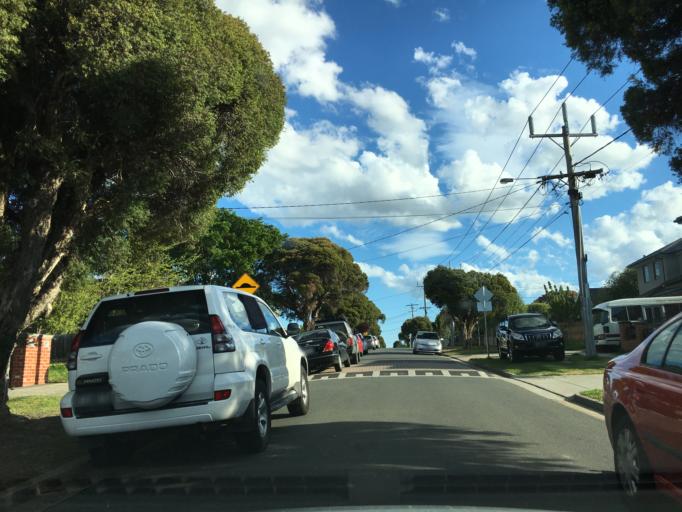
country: AU
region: Victoria
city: Clayton
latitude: -37.9007
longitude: 145.1130
